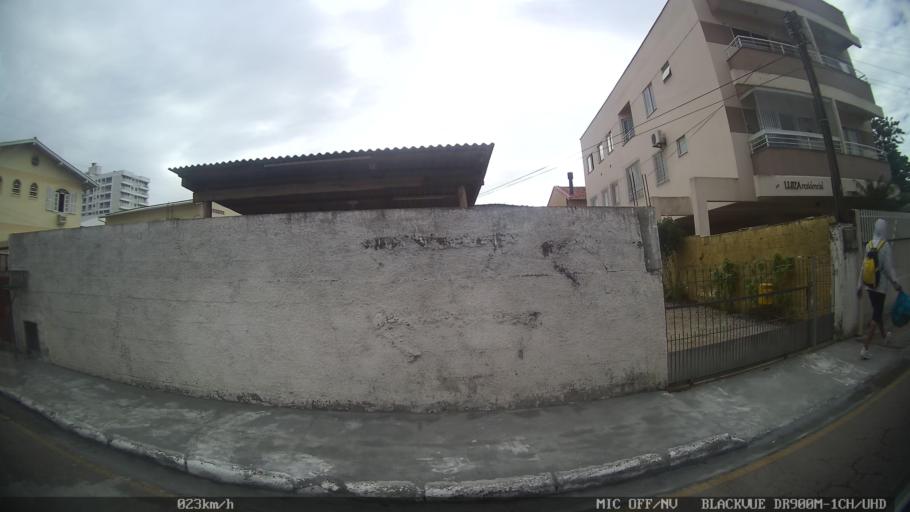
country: BR
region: Santa Catarina
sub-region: Sao Jose
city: Campinas
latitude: -27.5785
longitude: -48.6222
